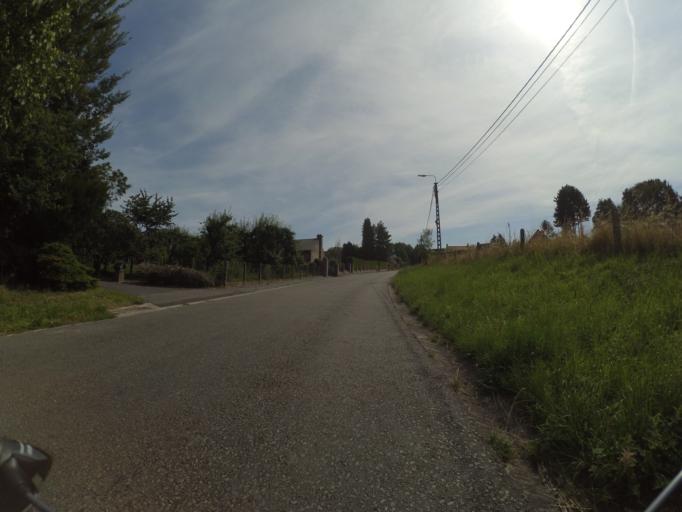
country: BE
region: Wallonia
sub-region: Province du Hainaut
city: Frasnes-lez-Anvaing
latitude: 50.7155
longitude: 3.6220
